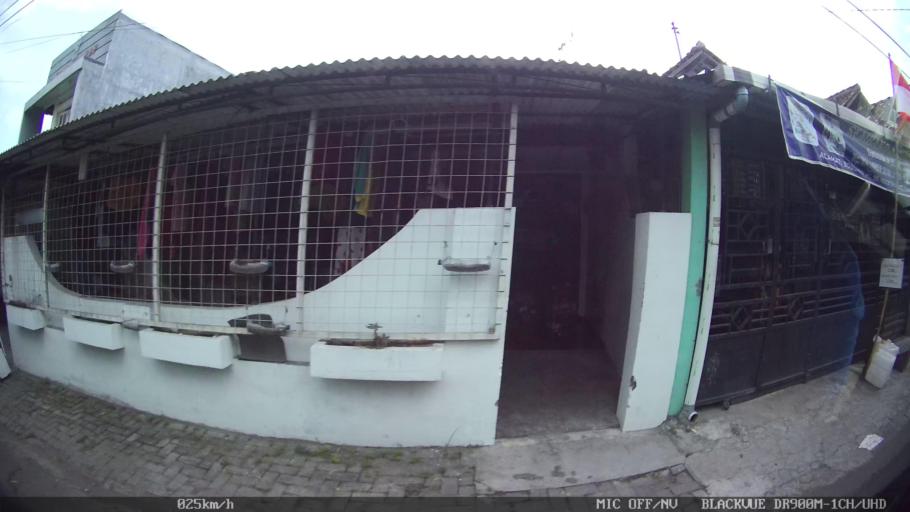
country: ID
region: Daerah Istimewa Yogyakarta
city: Gamping Lor
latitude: -7.8099
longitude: 110.3404
